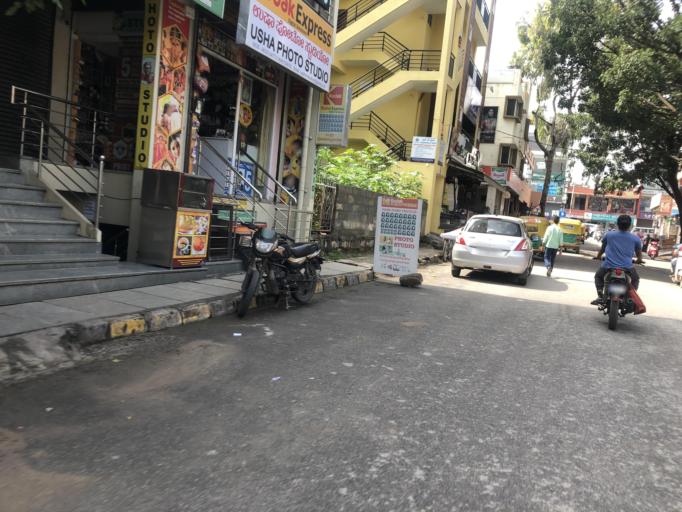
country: IN
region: Karnataka
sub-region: Bangalore Urban
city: Bangalore
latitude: 12.9039
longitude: 77.5211
